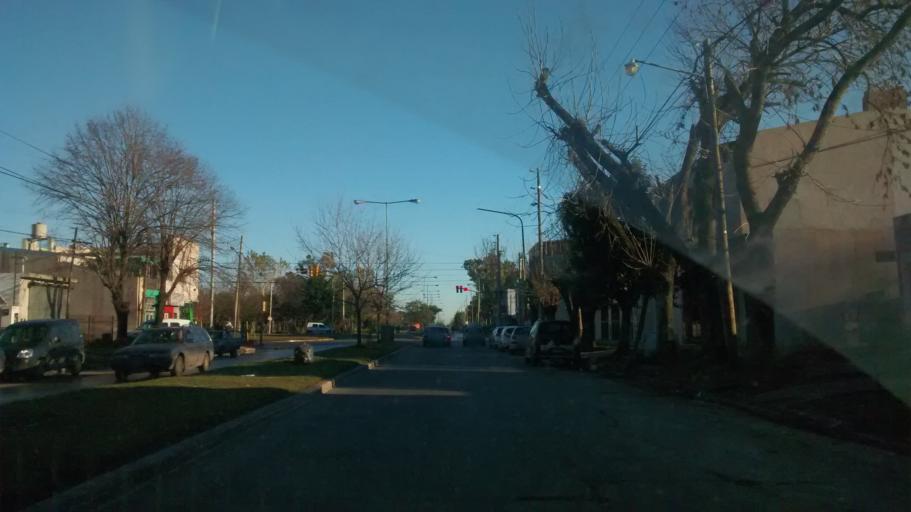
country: AR
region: Buenos Aires
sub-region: Partido de La Plata
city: La Plata
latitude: -34.9555
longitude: -57.9783
